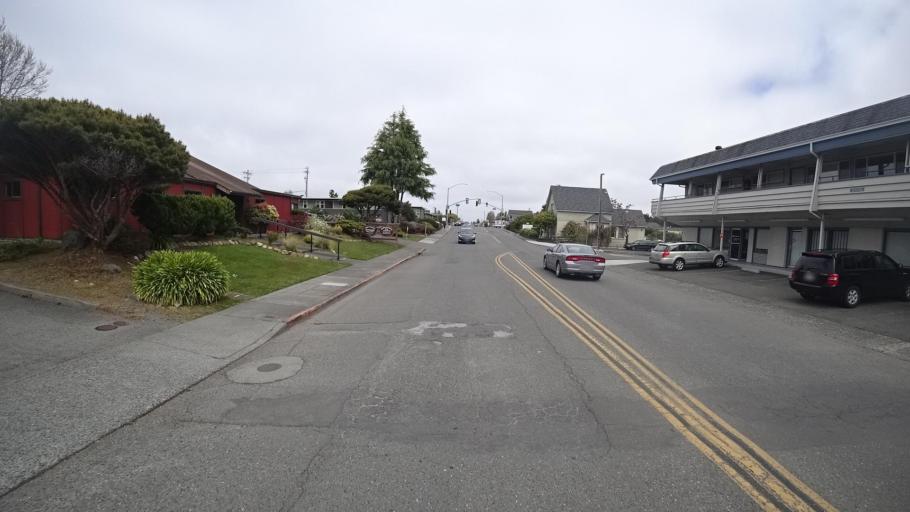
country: US
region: California
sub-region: Humboldt County
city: Myrtletown
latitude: 40.7851
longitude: -124.1397
